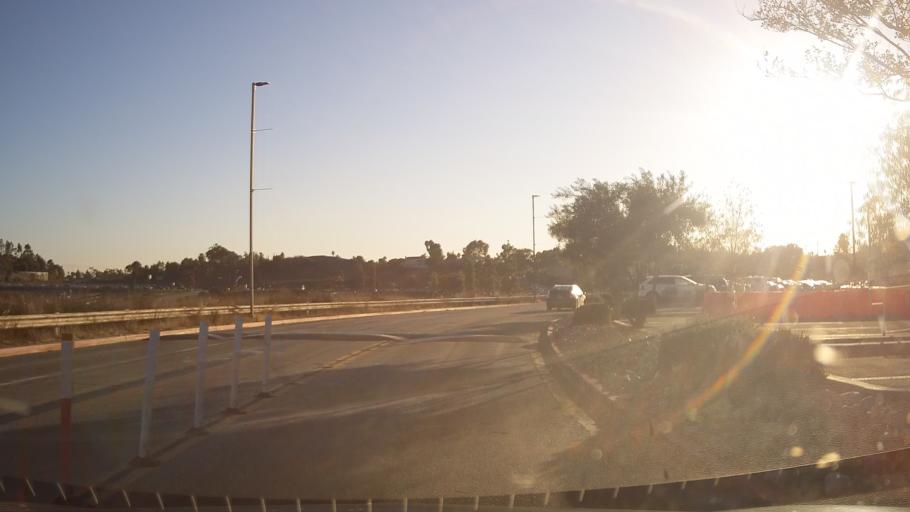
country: US
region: California
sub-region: San Diego County
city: Santee
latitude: 32.8157
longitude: -117.0029
